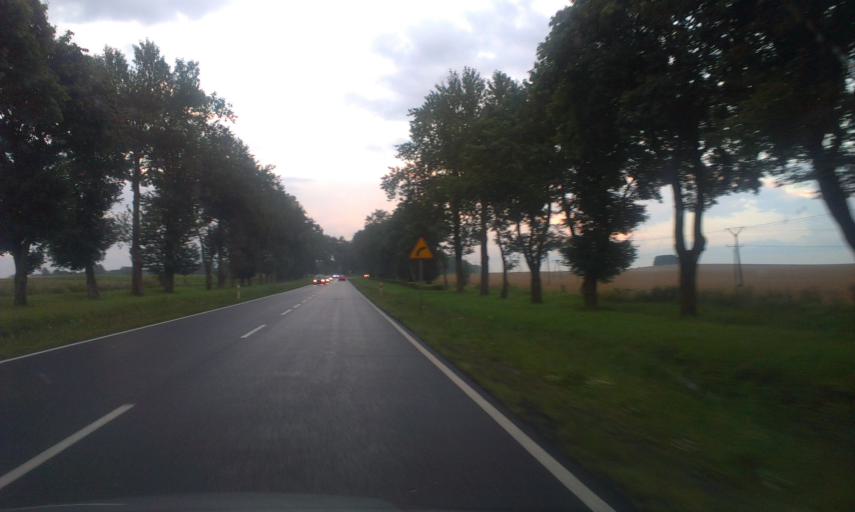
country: PL
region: West Pomeranian Voivodeship
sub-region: Koszalin
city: Koszalin
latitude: 54.1541
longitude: 16.2367
